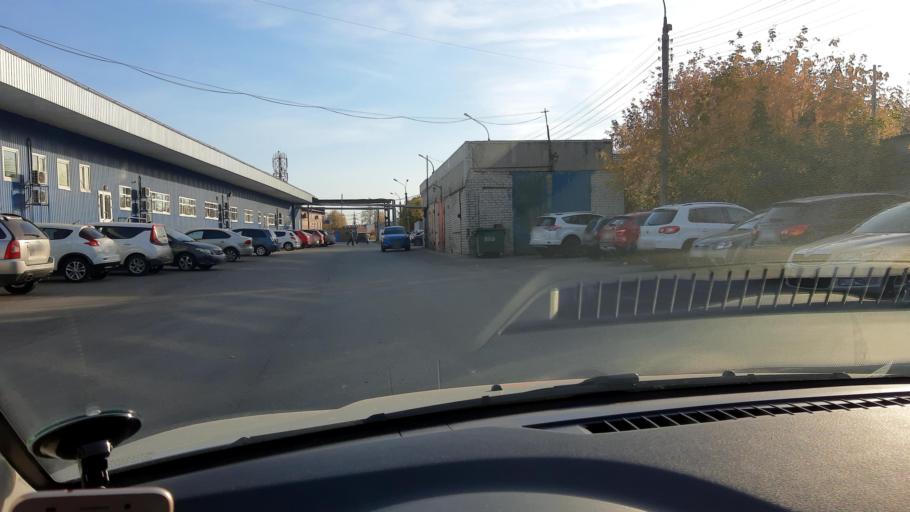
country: RU
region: Nizjnij Novgorod
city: Nizhniy Novgorod
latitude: 56.2591
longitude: 43.9157
